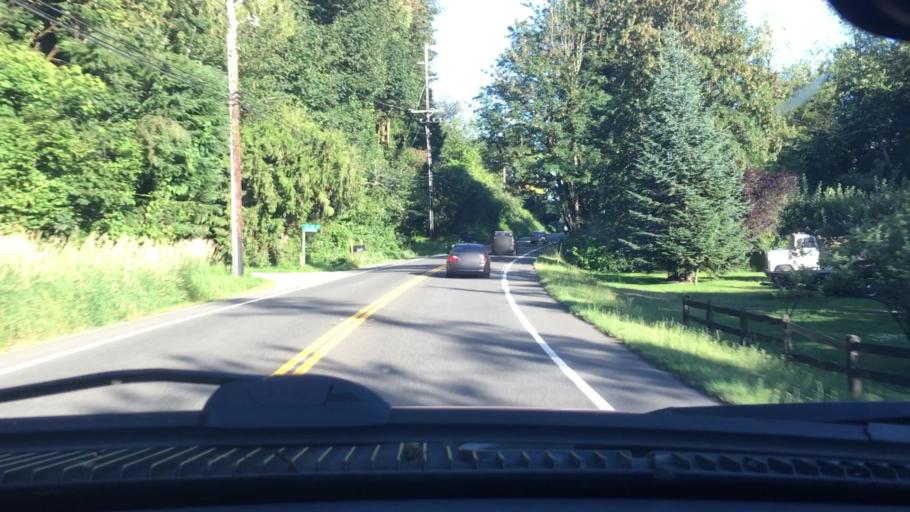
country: US
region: Washington
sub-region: King County
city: Mirrormont
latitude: 47.4571
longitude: -122.0017
